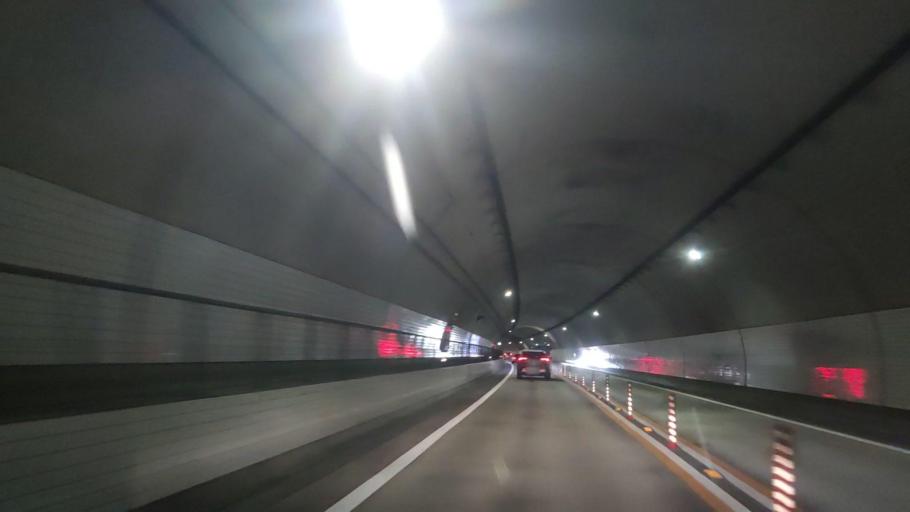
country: JP
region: Kyoto
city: Miyazu
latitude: 35.5630
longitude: 135.1215
